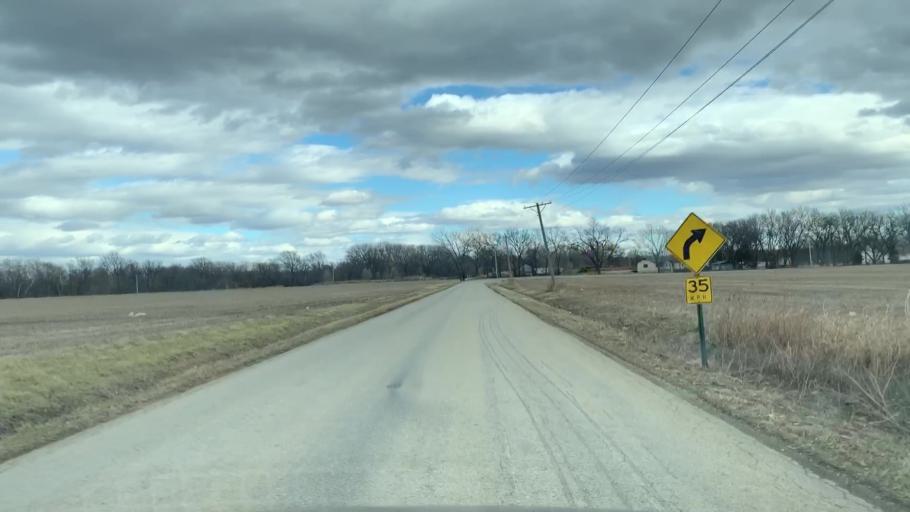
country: US
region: Kansas
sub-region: Allen County
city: Humboldt
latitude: 37.8129
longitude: -95.4553
